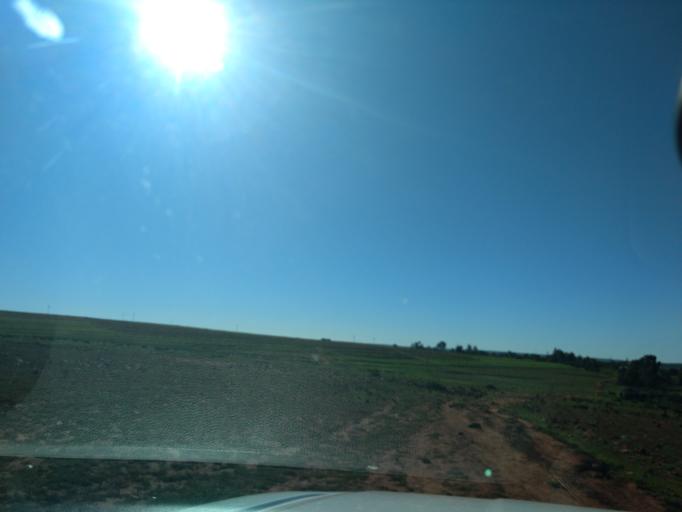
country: LS
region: Berea
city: Teyateyaneng
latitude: -29.3684
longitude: 27.7867
